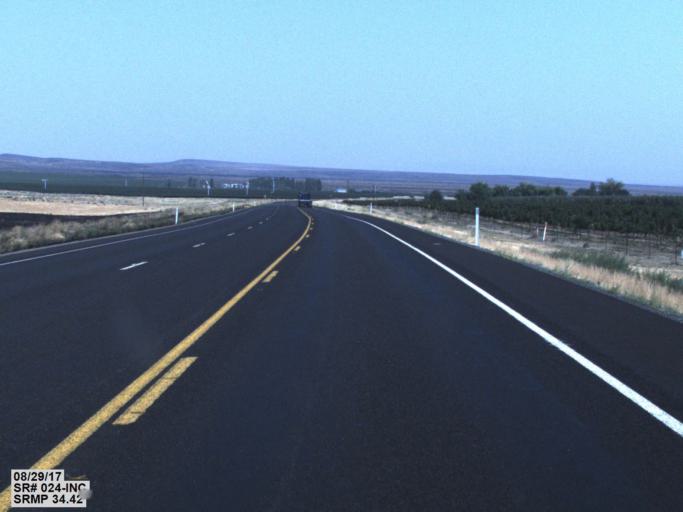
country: US
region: Washington
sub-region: Grant County
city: Desert Aire
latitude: 46.5596
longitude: -119.8071
